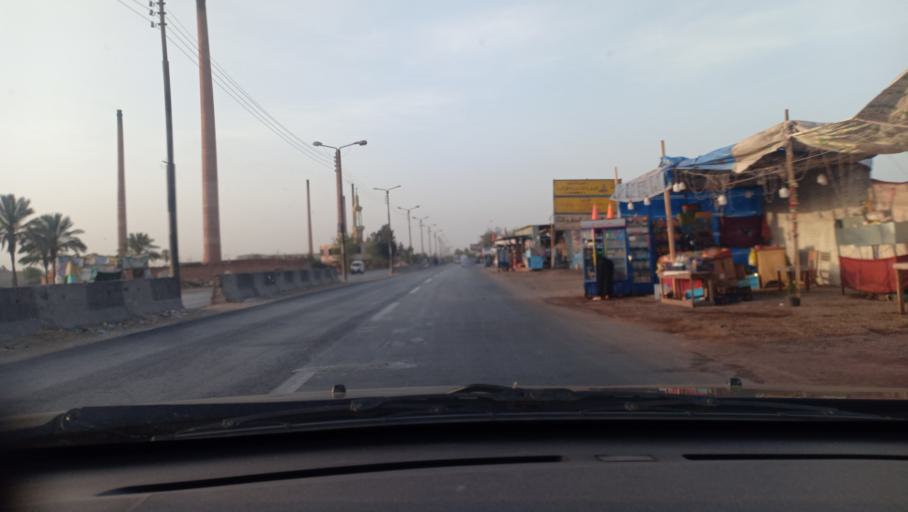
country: EG
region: Muhafazat al Gharbiyah
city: Zifta
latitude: 30.6100
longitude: 31.2757
